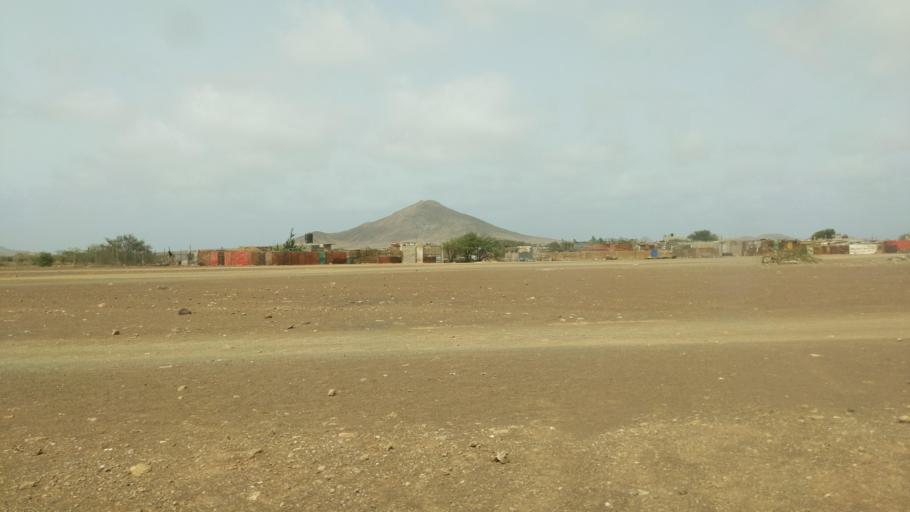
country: CV
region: Sal
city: Espargos
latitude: 16.7744
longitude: -22.9479
